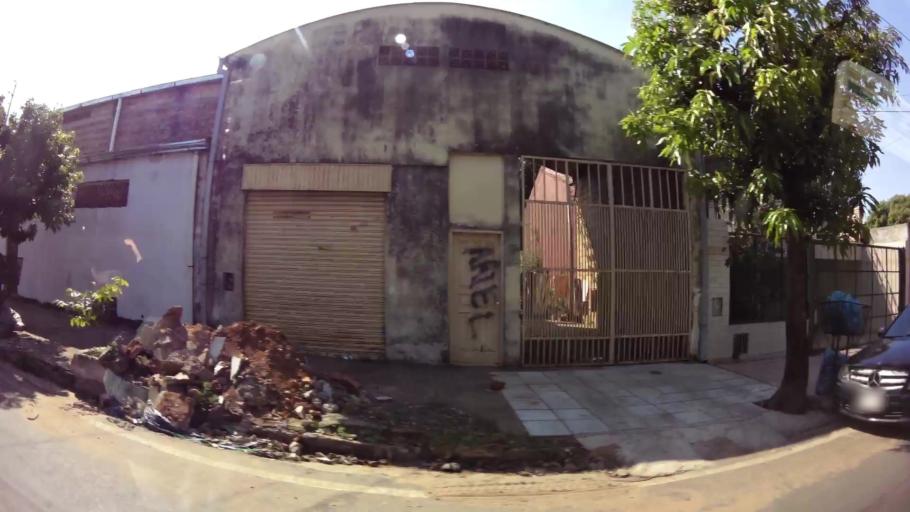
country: PY
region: Central
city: San Lorenzo
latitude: -25.3516
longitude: -57.5057
